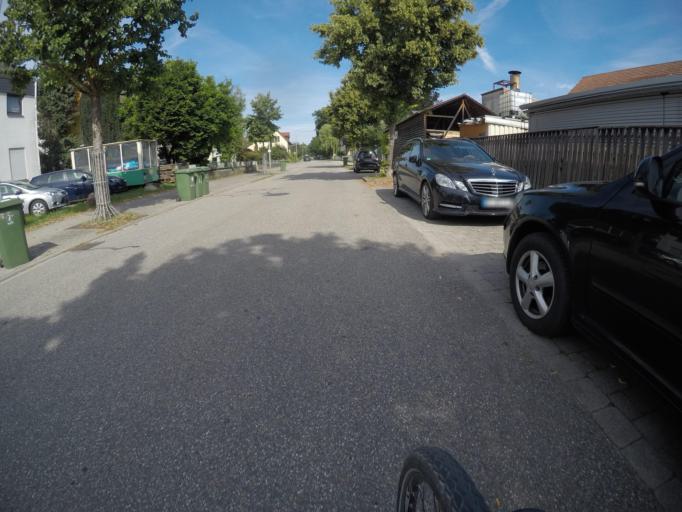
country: DE
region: Baden-Wuerttemberg
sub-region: Karlsruhe Region
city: Otisheim
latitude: 48.9643
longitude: 8.8043
